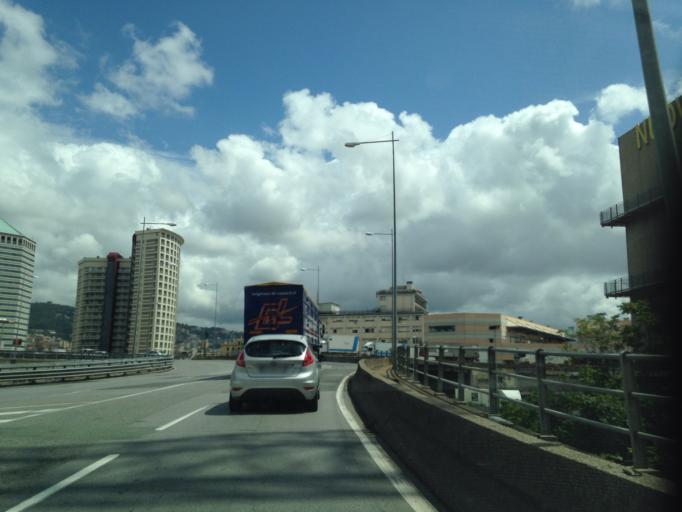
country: IT
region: Liguria
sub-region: Provincia di Genova
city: San Teodoro
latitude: 44.4081
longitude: 8.9024
